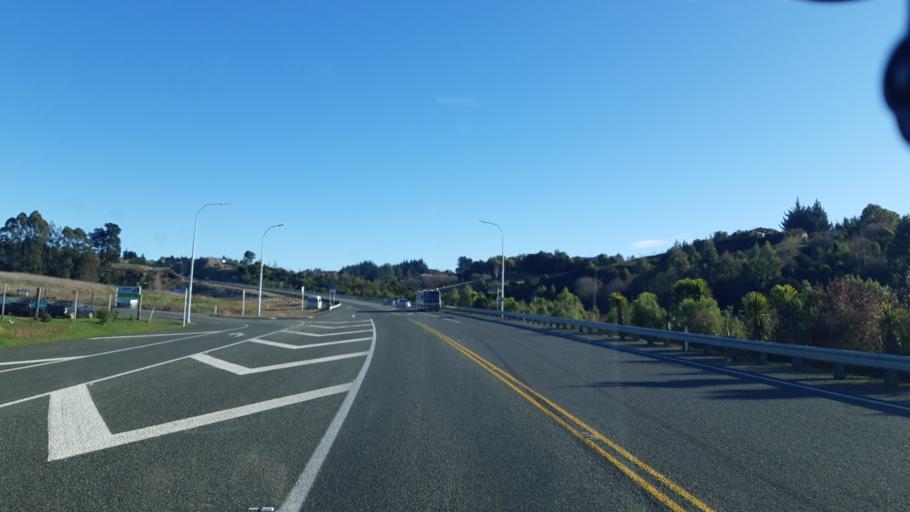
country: NZ
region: Tasman
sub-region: Tasman District
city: Mapua
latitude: -41.2513
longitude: 173.0691
